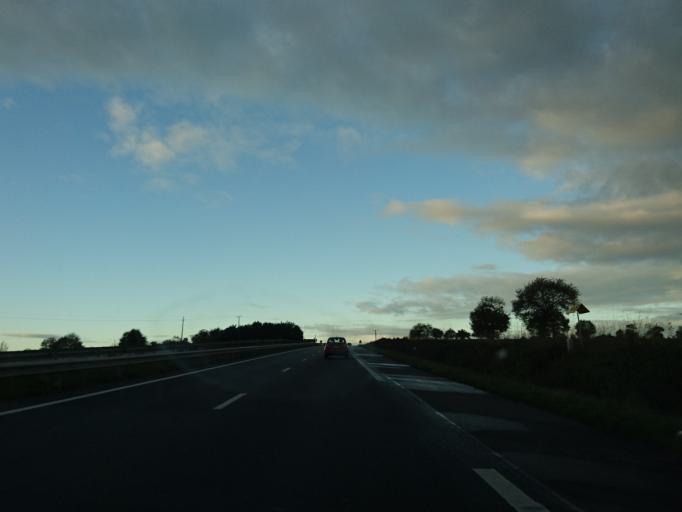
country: FR
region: Brittany
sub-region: Departement d'Ille-et-Vilaine
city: Quedillac
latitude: 48.2265
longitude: -2.1154
